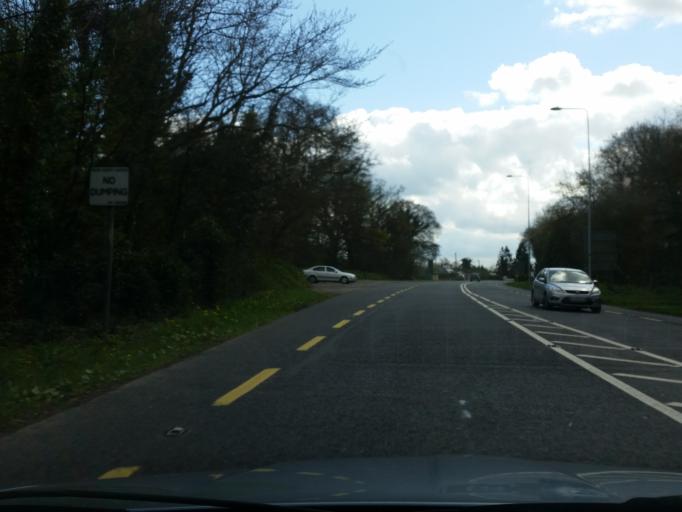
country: IE
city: Kentstown
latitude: 53.6397
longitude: -6.4979
